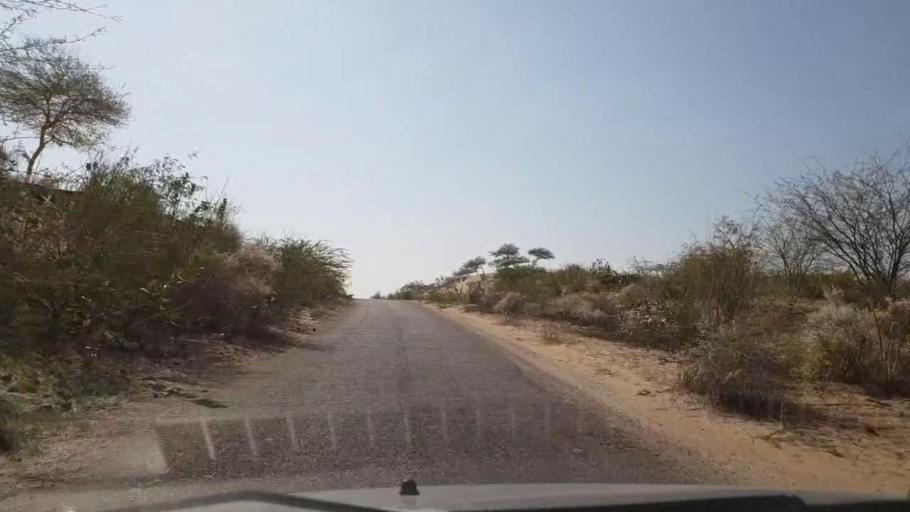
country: PK
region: Sindh
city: Diplo
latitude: 24.5425
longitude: 69.6465
